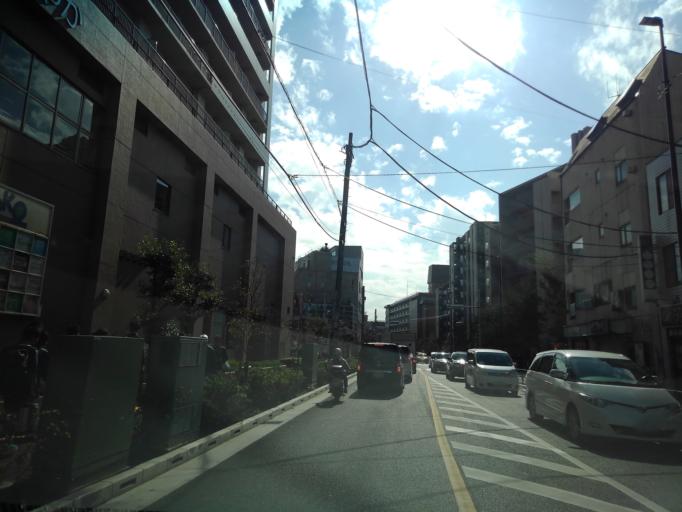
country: JP
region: Tokyo
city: Chofugaoka
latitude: 35.6492
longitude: 139.5584
